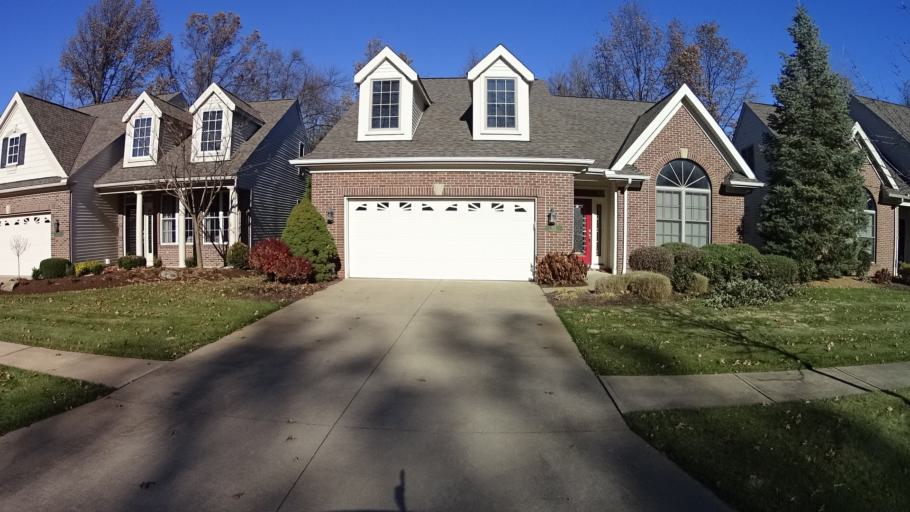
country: US
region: Ohio
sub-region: Lorain County
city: Avon Center
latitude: 41.4868
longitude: -81.9989
